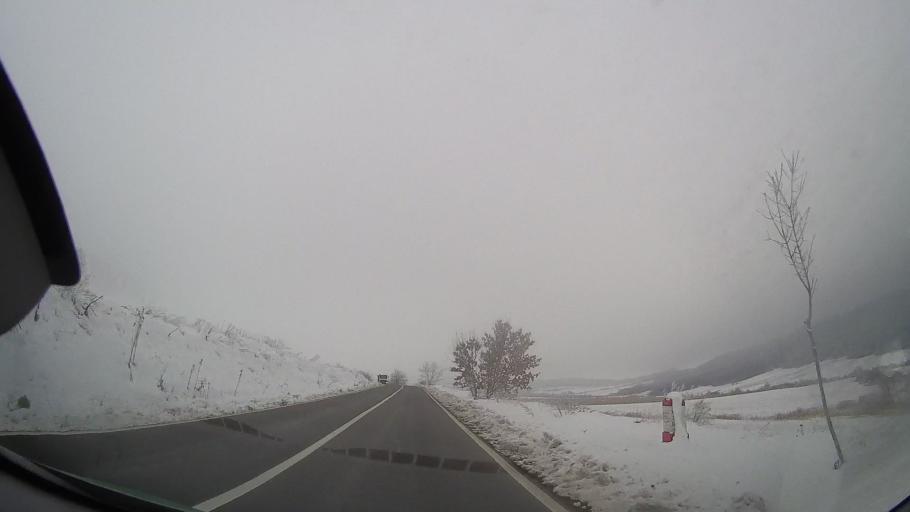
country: RO
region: Neamt
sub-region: Comuna Poenari
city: Poienari
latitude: 46.8722
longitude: 27.1415
